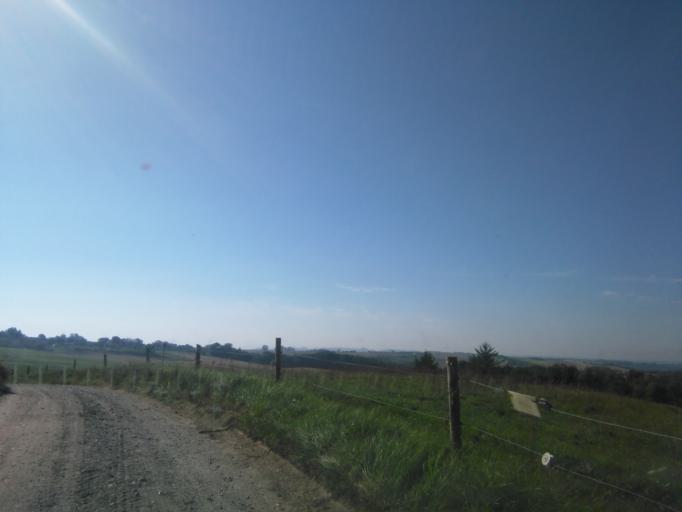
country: DK
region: Central Jutland
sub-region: Syddjurs Kommune
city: Ronde
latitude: 56.2022
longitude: 10.5207
